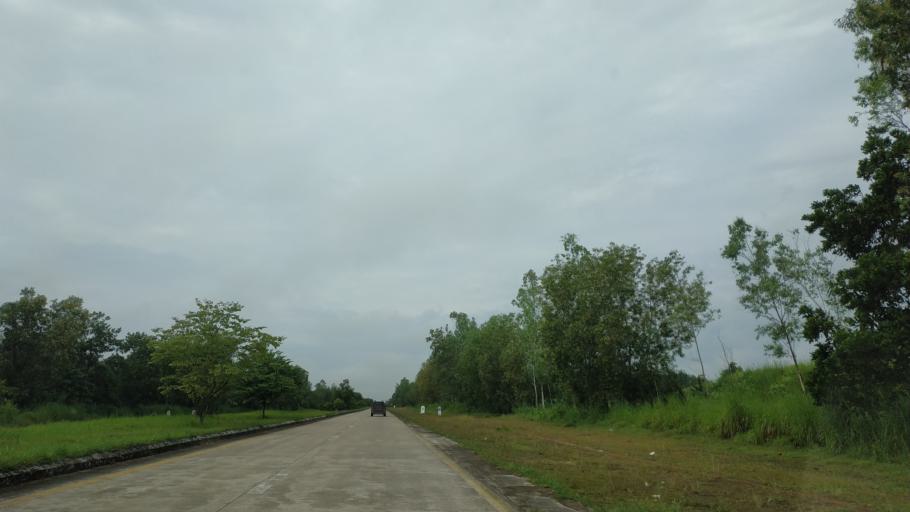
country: MM
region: Bago
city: Bago
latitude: 17.4454
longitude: 96.4129
